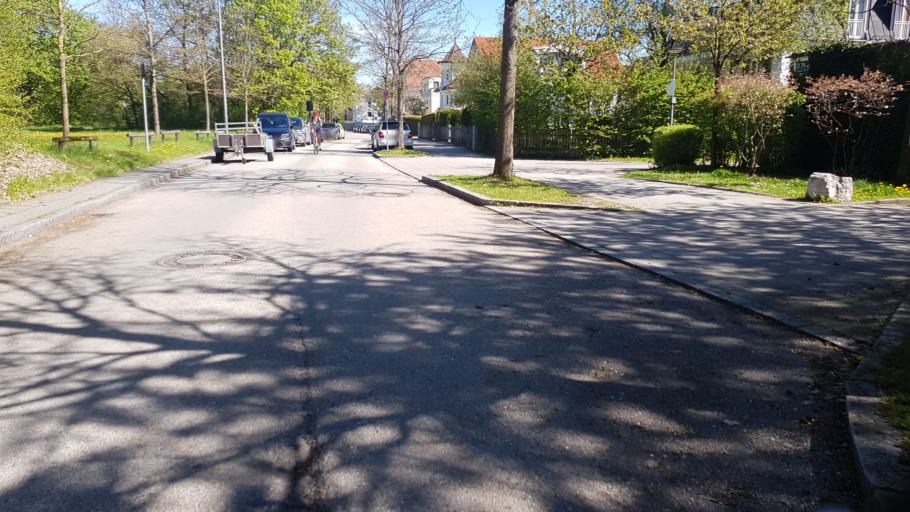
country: DE
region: Bavaria
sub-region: Upper Bavaria
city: Pasing
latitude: 48.1709
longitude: 11.5016
